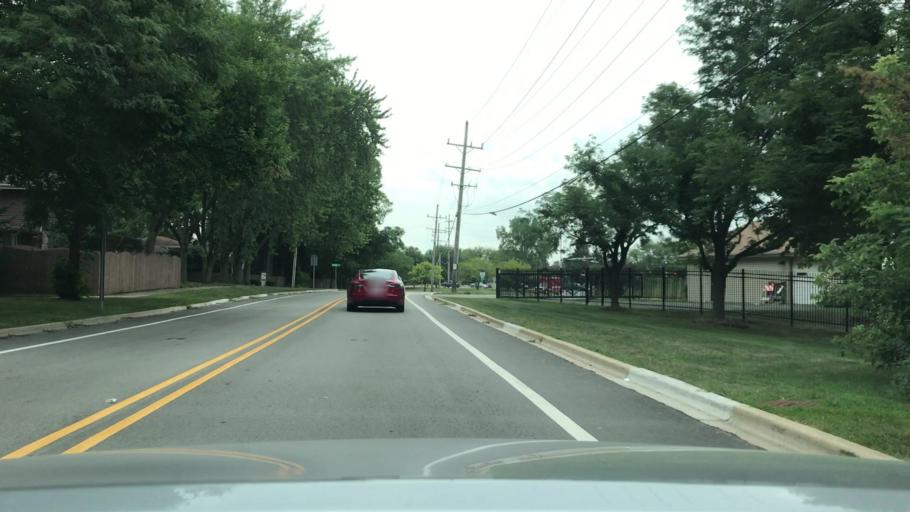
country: US
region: Illinois
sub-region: DuPage County
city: Darien
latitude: 41.7444
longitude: -87.9898
